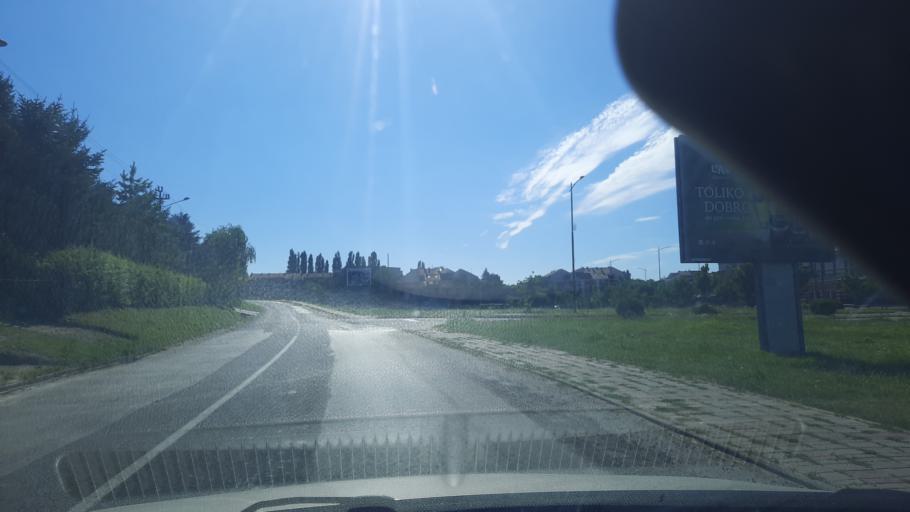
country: RS
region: Autonomna Pokrajina Vojvodina
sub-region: Juznobacki Okrug
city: Beocin
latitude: 45.2088
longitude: 19.7287
